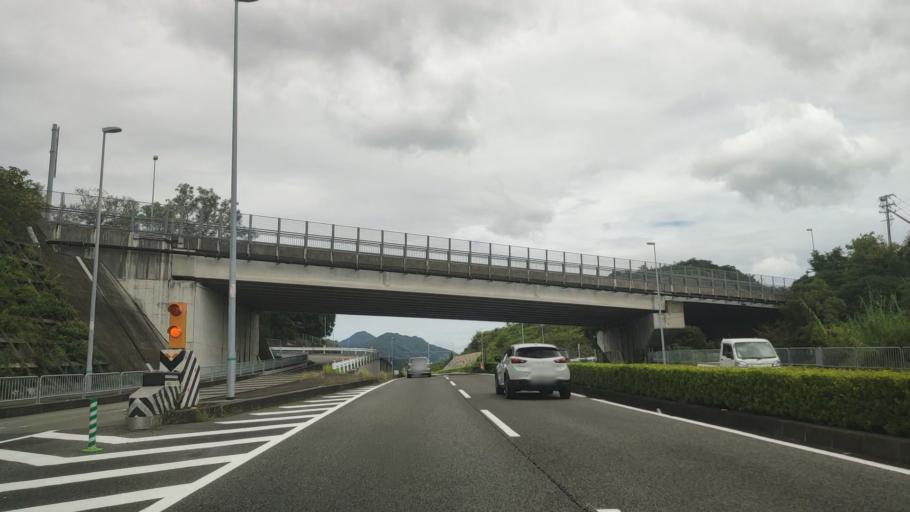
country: JP
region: Wakayama
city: Tanabe
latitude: 33.7319
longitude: 135.4005
